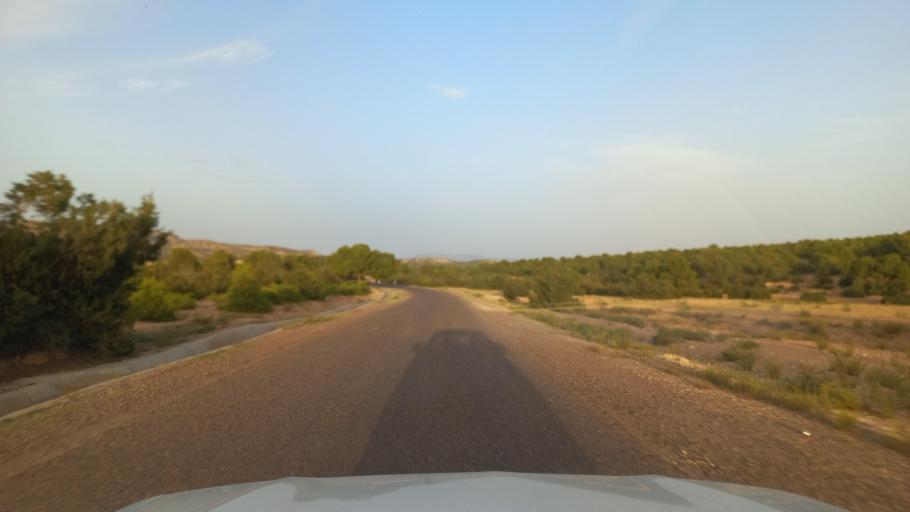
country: TN
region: Al Qasrayn
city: Sbiba
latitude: 35.4099
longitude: 8.9183
